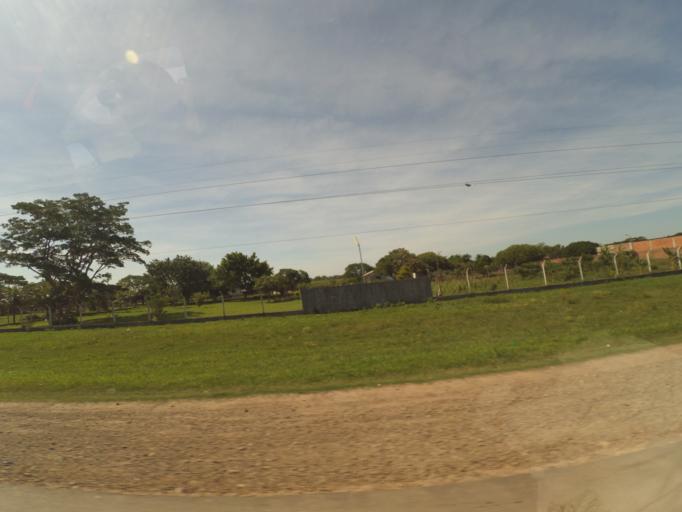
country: BO
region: Santa Cruz
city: San Julian
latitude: -17.7455
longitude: -62.9570
